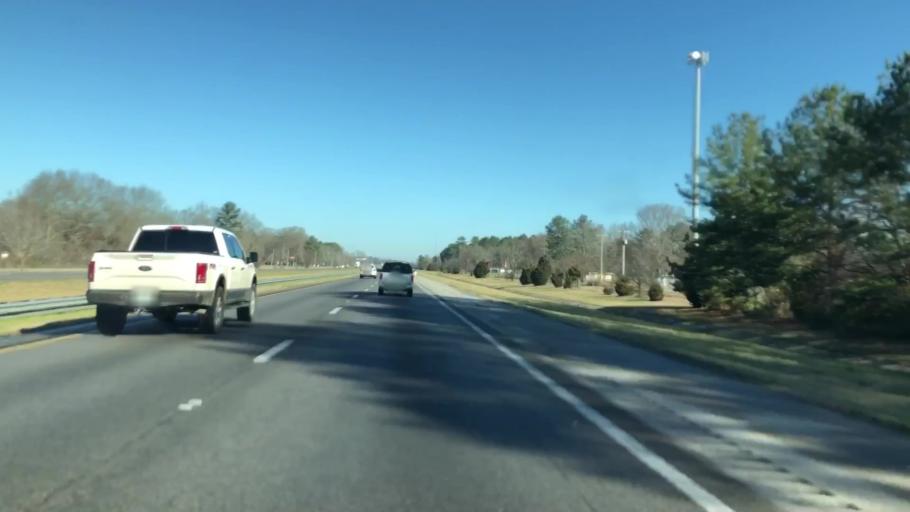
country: US
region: Alabama
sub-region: Limestone County
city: Athens
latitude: 34.8640
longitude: -86.9251
